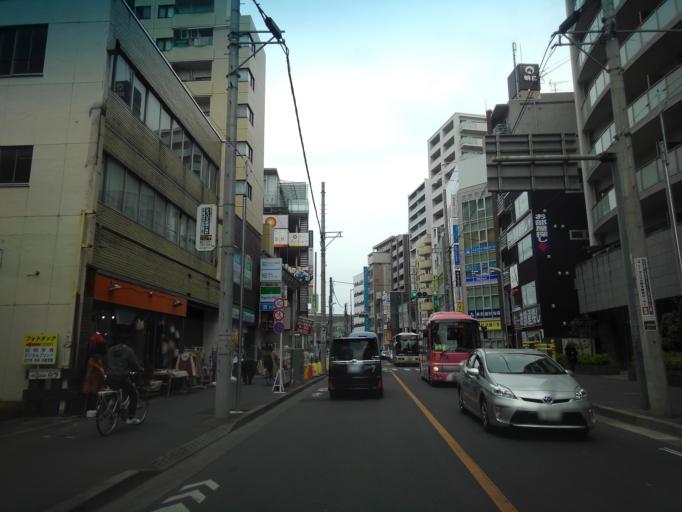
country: JP
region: Tokyo
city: Kokubunji
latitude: 35.6994
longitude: 139.5067
